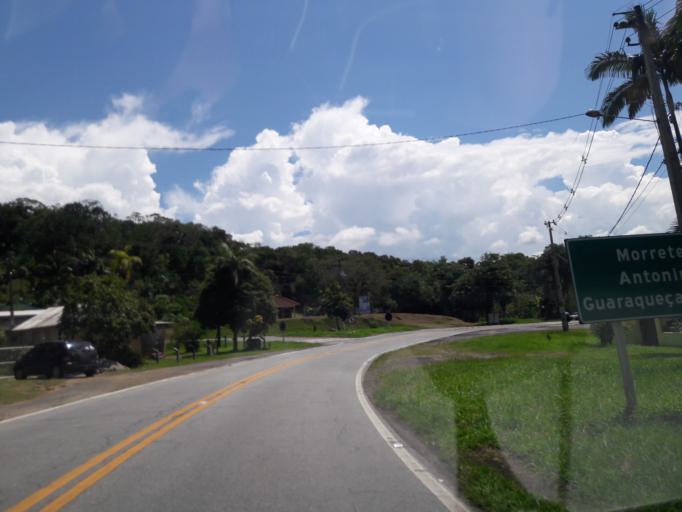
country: BR
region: Parana
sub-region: Antonina
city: Antonina
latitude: -25.5244
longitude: -48.7954
